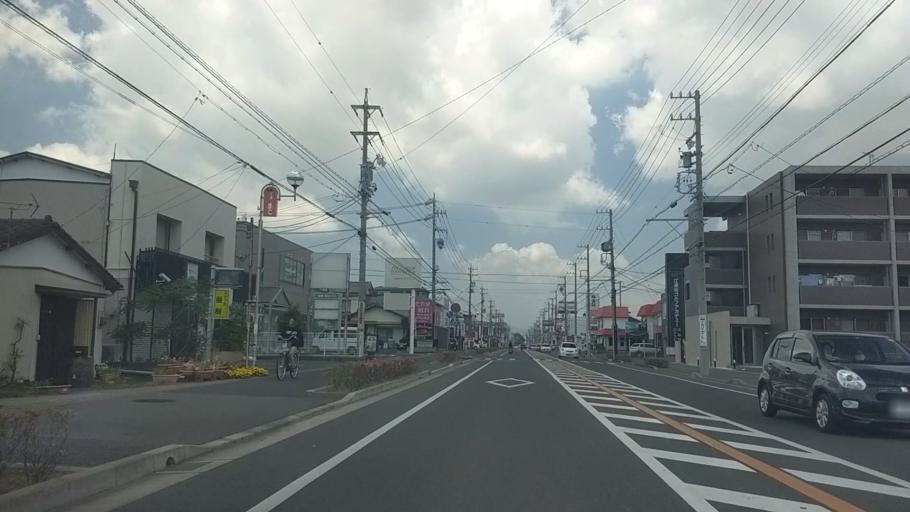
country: JP
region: Shizuoka
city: Hamamatsu
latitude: 34.7594
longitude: 137.7260
